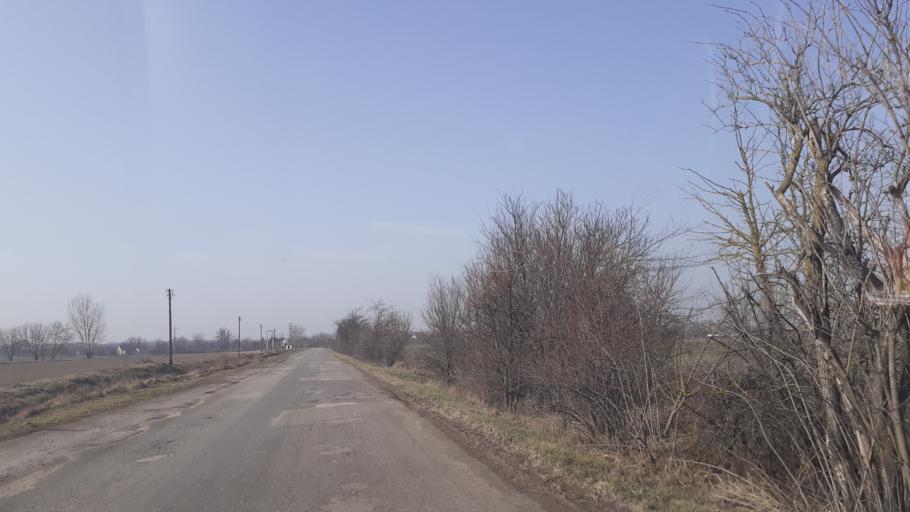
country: HU
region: Pest
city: Dabas
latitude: 47.0668
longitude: 19.2627
